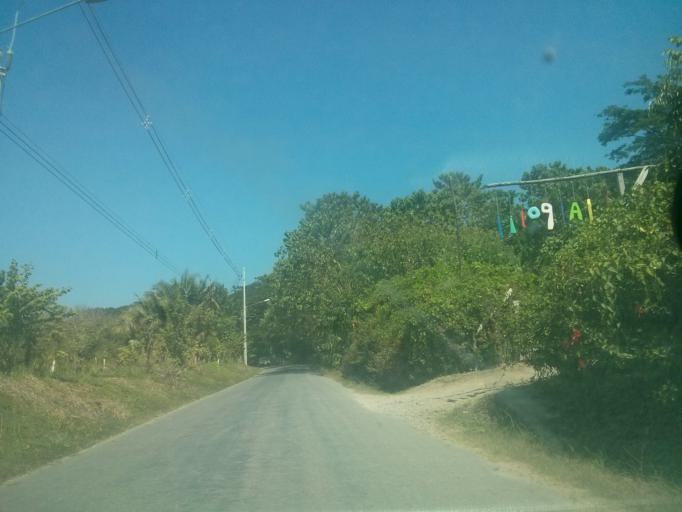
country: CR
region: Puntarenas
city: Paquera
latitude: 9.6225
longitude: -85.1463
